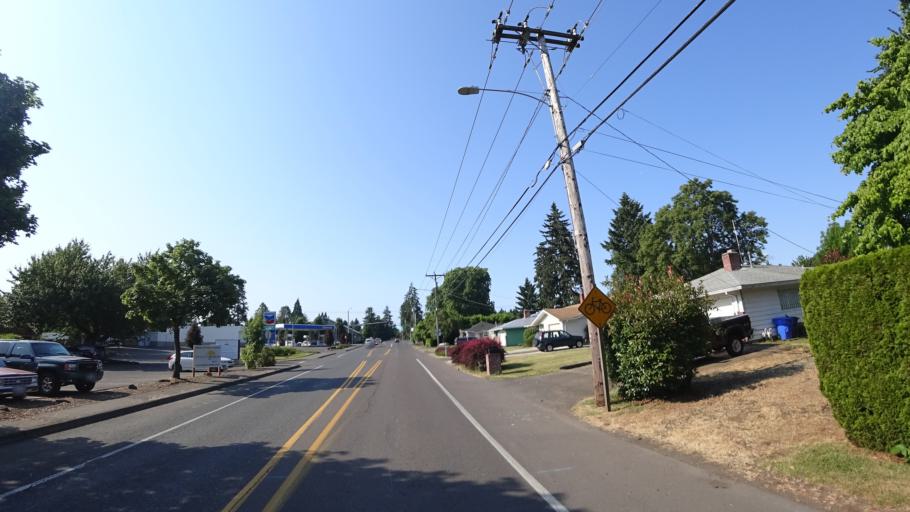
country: US
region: Oregon
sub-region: Clackamas County
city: Oatfield
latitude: 45.4492
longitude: -122.5990
